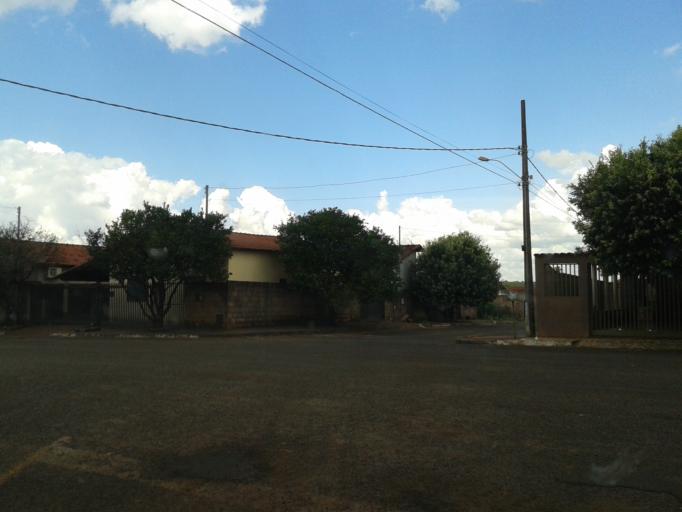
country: BR
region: Minas Gerais
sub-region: Capinopolis
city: Capinopolis
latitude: -18.6920
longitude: -49.5648
